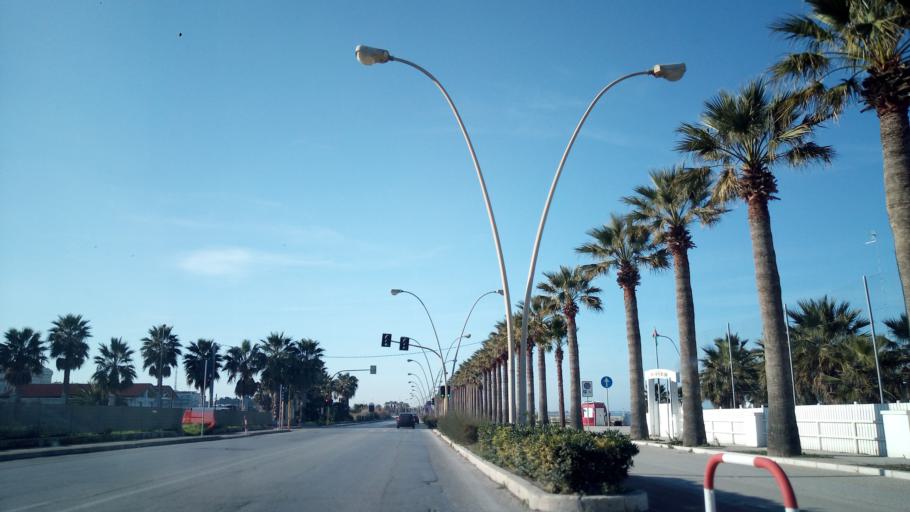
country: IT
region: Apulia
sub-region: Provincia di Barletta - Andria - Trani
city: Barletta
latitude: 41.3244
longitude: 16.2720
